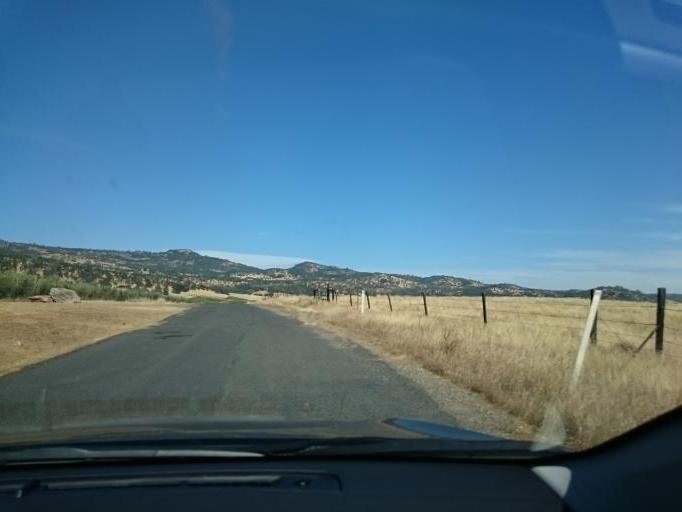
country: US
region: California
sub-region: Calaveras County
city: Copperopolis
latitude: 38.0491
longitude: -120.7157
